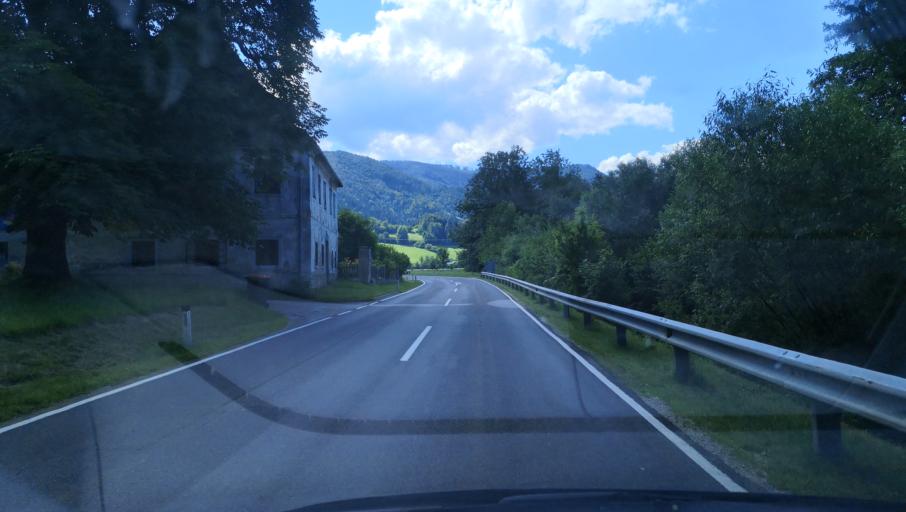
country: AT
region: Lower Austria
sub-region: Politischer Bezirk Scheibbs
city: Gresten
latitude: 47.9595
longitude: 15.0293
